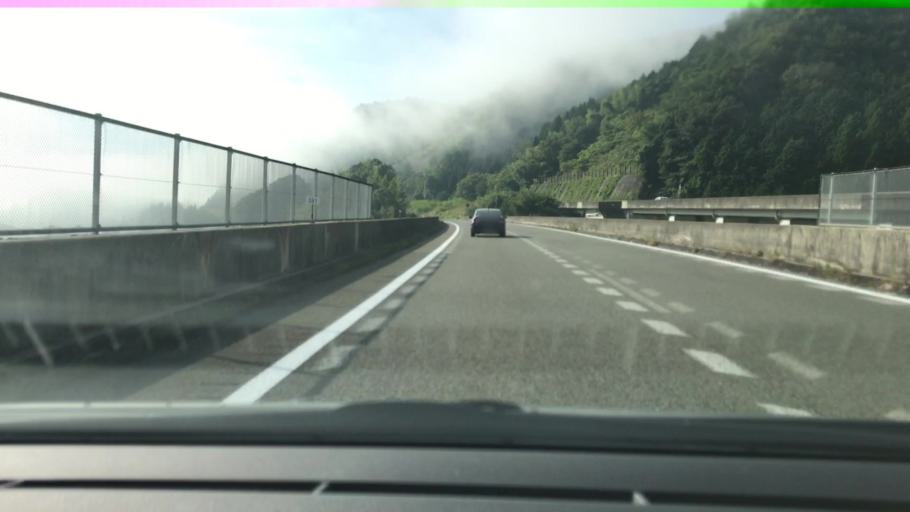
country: JP
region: Hyogo
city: Sasayama
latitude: 35.1131
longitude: 135.1658
